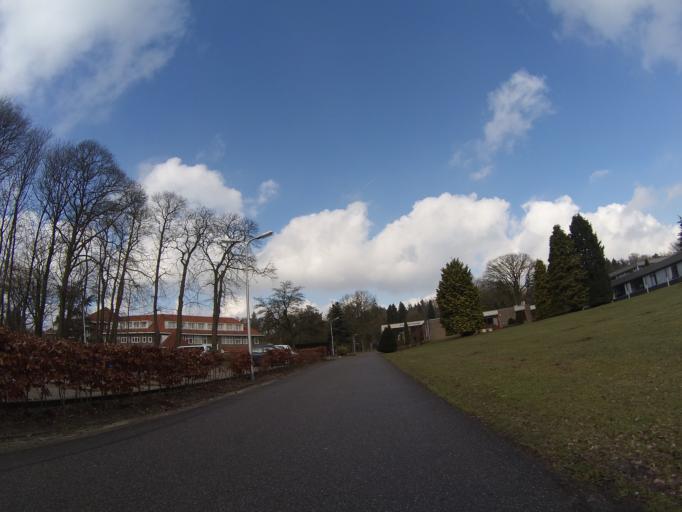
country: NL
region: Utrecht
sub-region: Gemeente Amersfoort
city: Amersfoort
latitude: 52.1332
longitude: 5.3367
